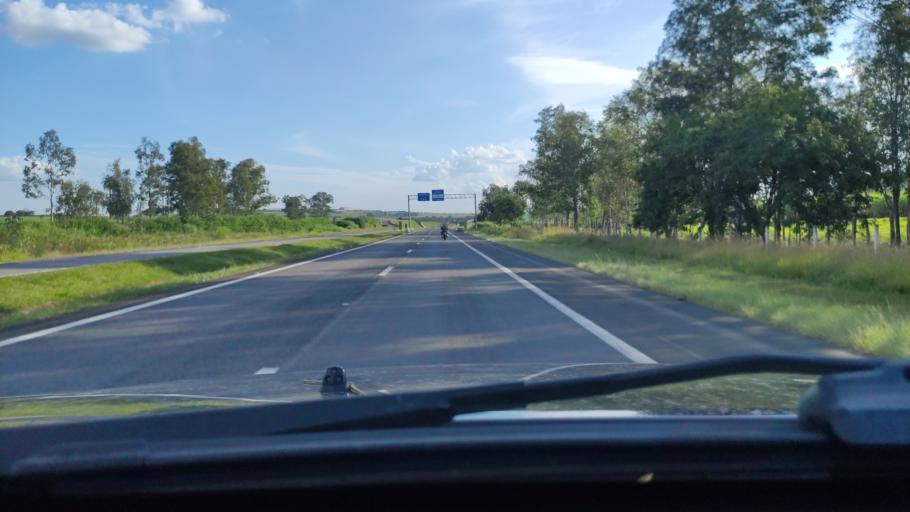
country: BR
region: Sao Paulo
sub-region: Mogi-Mirim
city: Mogi Mirim
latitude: -22.4527
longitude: -46.8922
